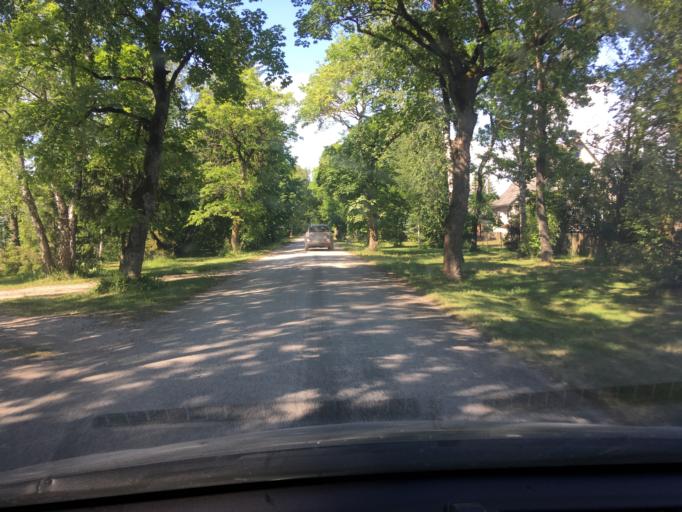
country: EE
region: Laeaene
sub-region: Lihula vald
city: Lihula
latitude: 58.5837
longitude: 23.5372
